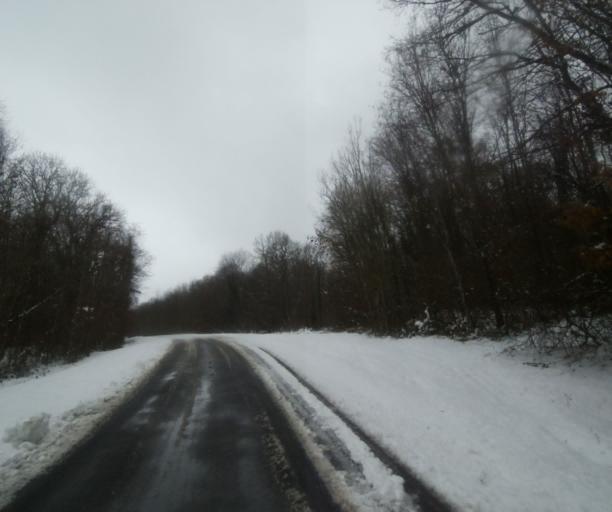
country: FR
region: Champagne-Ardenne
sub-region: Departement de la Haute-Marne
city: Laneuville-a-Remy
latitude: 48.5101
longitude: 4.8971
